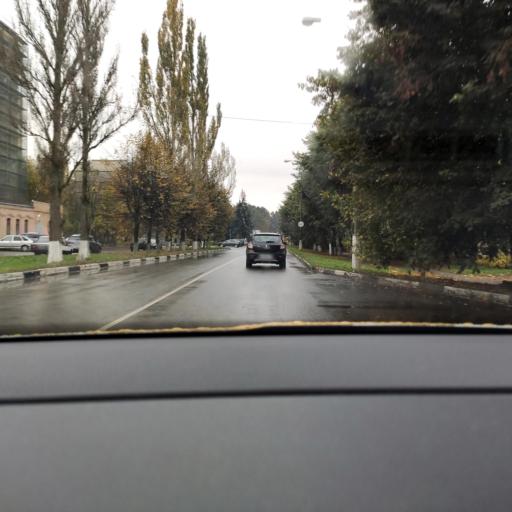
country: RU
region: Moskovskaya
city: Ivanteyevka
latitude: 55.9672
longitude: 37.9072
